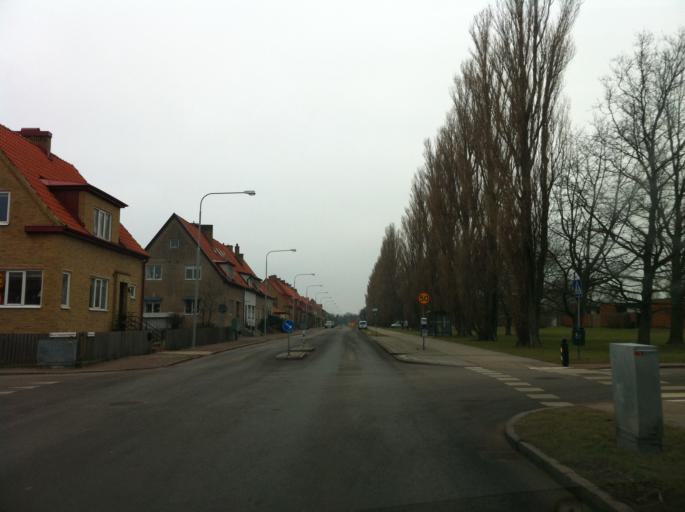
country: SE
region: Skane
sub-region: Landskrona
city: Landskrona
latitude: 55.8959
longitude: 12.8082
